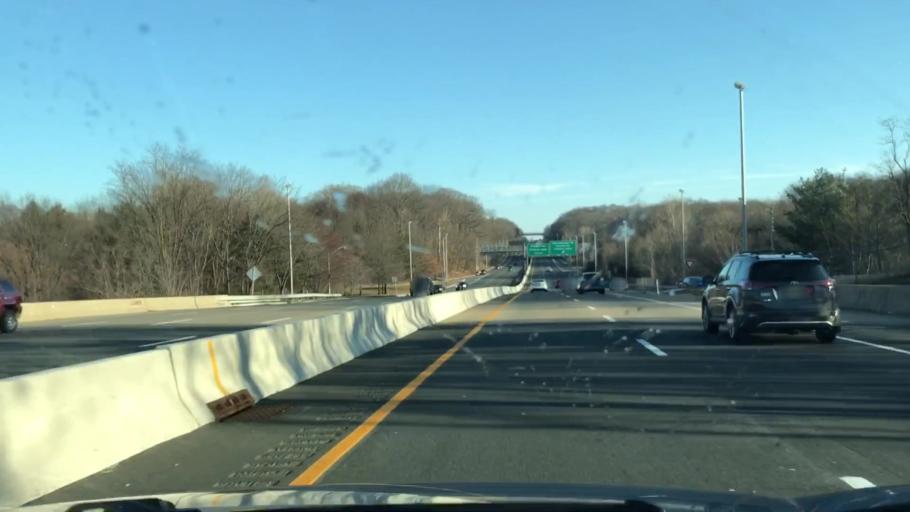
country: US
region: New Jersey
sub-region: Bergen County
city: Franklin Lakes
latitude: 41.0183
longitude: -74.2191
